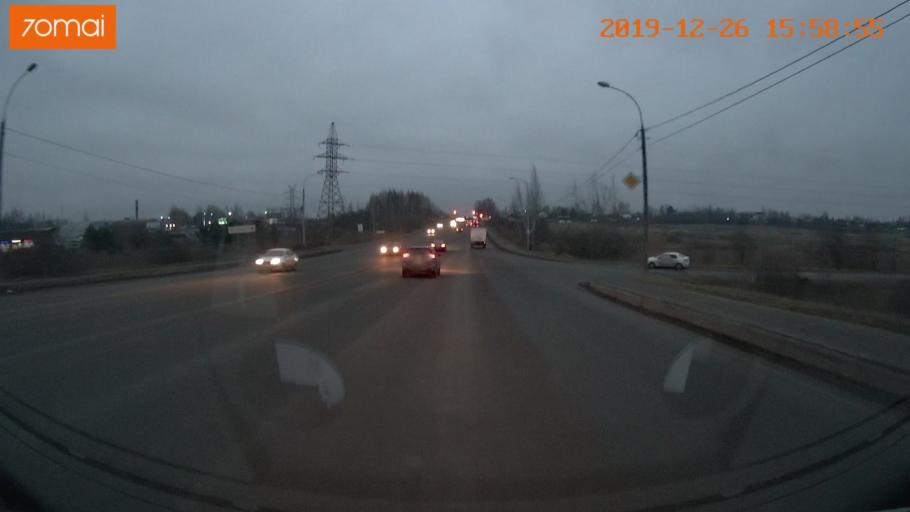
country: RU
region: Jaroslavl
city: Rybinsk
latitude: 58.0354
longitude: 38.8000
